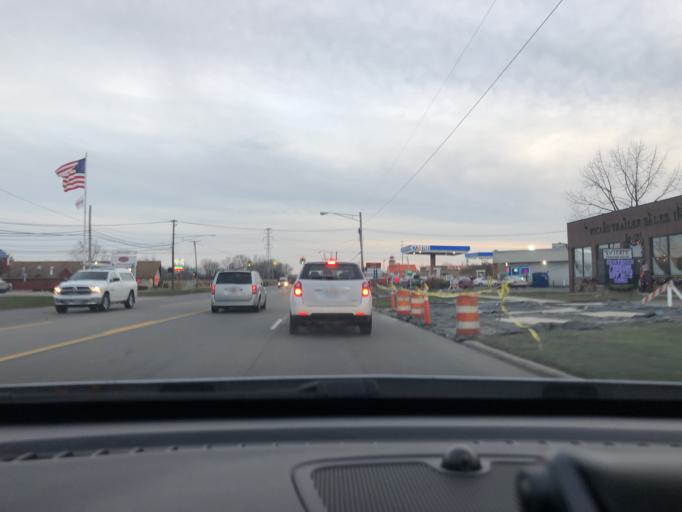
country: US
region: Michigan
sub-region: Wayne County
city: Allen Park
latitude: 42.2430
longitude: -83.2307
